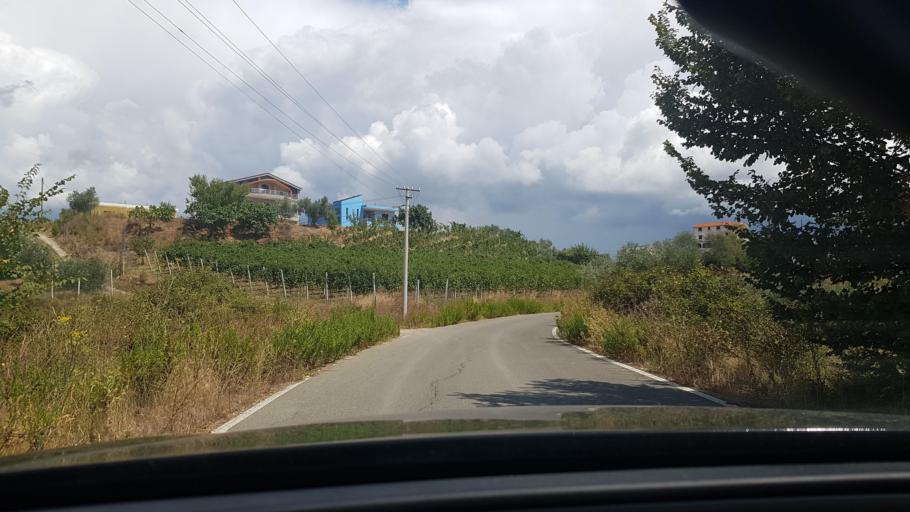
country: AL
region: Durres
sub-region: Rrethi i Durresit
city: Rrashbull
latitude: 41.2953
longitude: 19.5316
